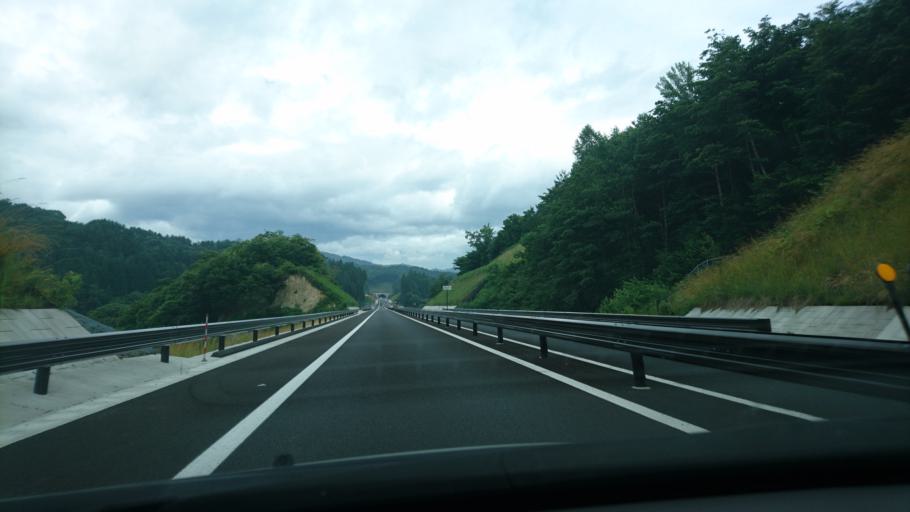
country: JP
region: Iwate
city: Miyako
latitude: 39.5566
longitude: 141.9260
